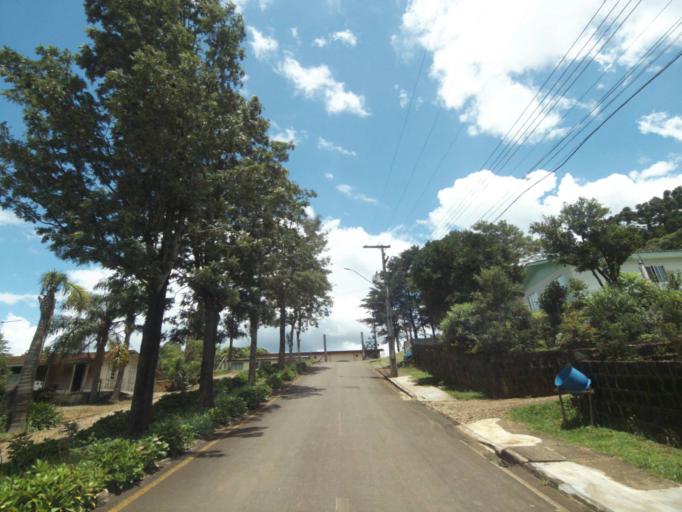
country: BR
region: Parana
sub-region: Uniao Da Vitoria
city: Uniao da Vitoria
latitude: -26.1603
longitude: -51.5561
